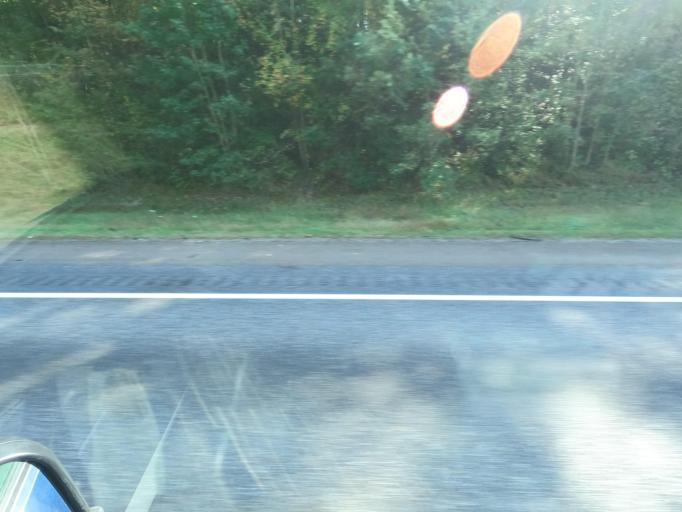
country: US
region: Tennessee
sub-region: Haywood County
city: Brownsville
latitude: 35.5278
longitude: -89.2583
